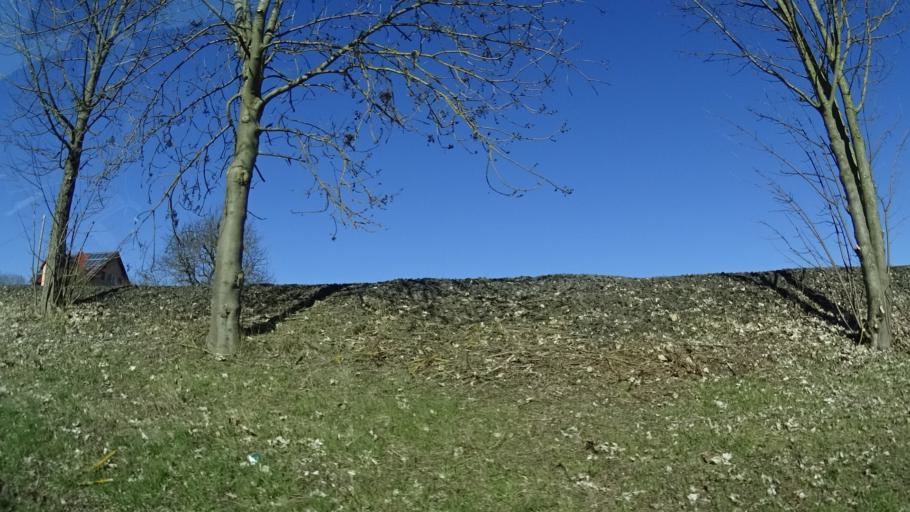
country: DE
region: Bavaria
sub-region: Regierungsbezirk Unterfranken
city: Stockheim
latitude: 50.4530
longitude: 10.2800
